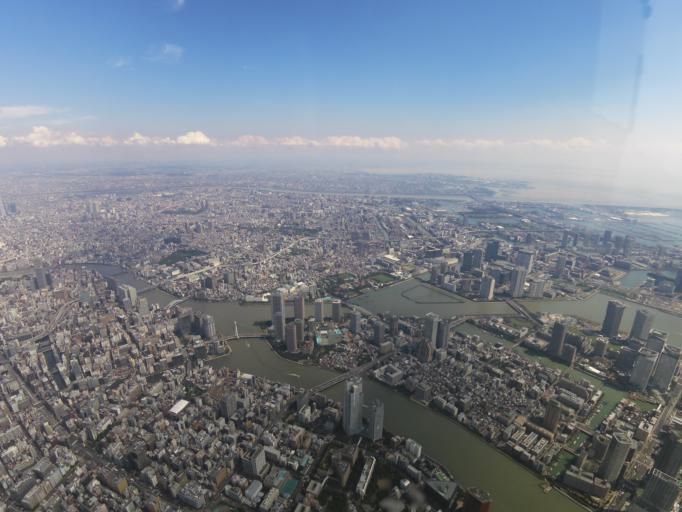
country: JP
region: Tokyo
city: Tokyo
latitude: 35.6668
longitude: 139.7693
